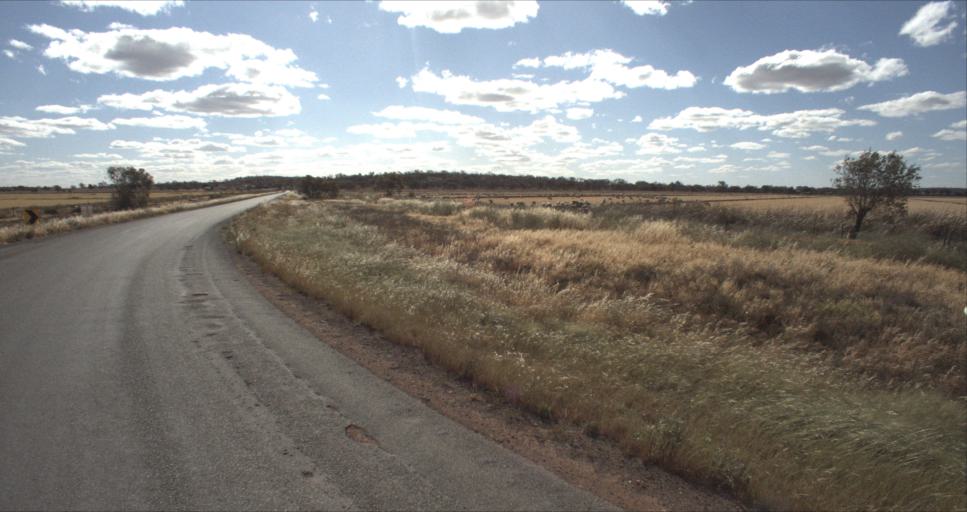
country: AU
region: New South Wales
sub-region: Leeton
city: Leeton
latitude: -34.4214
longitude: 146.2739
